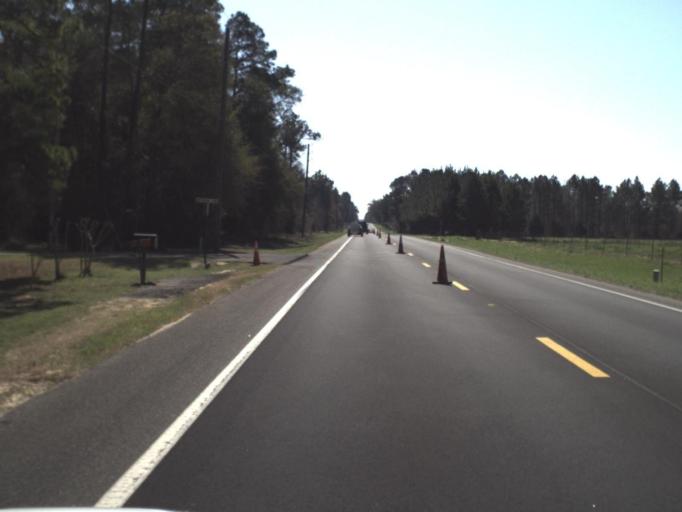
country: US
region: Florida
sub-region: Jackson County
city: Marianna
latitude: 30.6971
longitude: -85.1823
